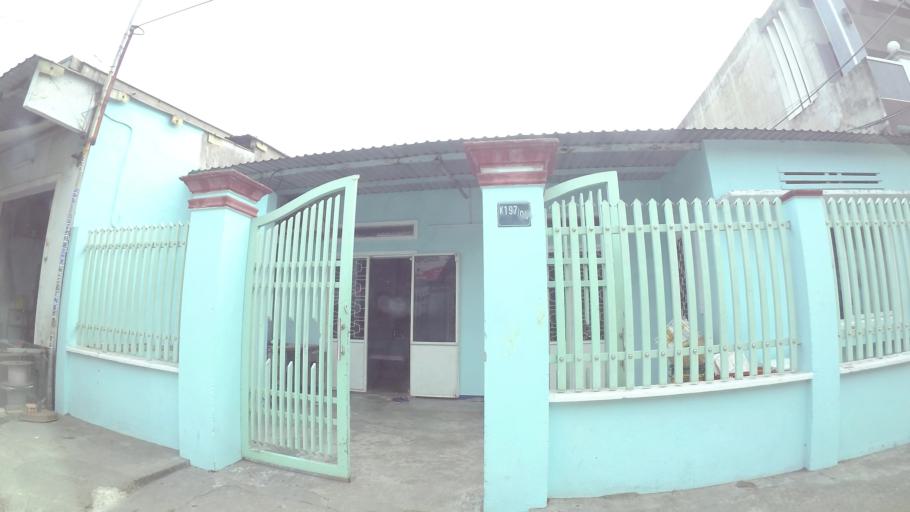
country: VN
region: Da Nang
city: Son Tra
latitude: 16.0920
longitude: 108.2440
